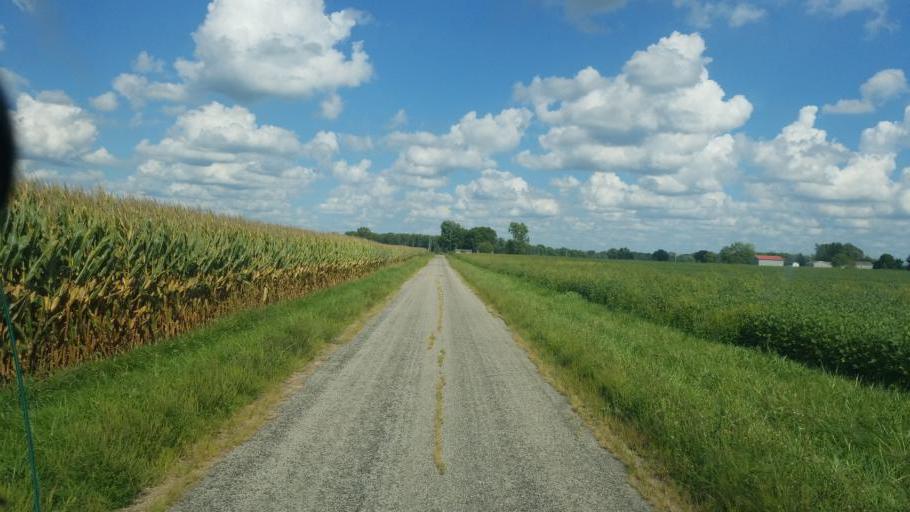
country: US
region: Ohio
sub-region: Union County
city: Richwood
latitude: 40.4659
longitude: -83.3322
